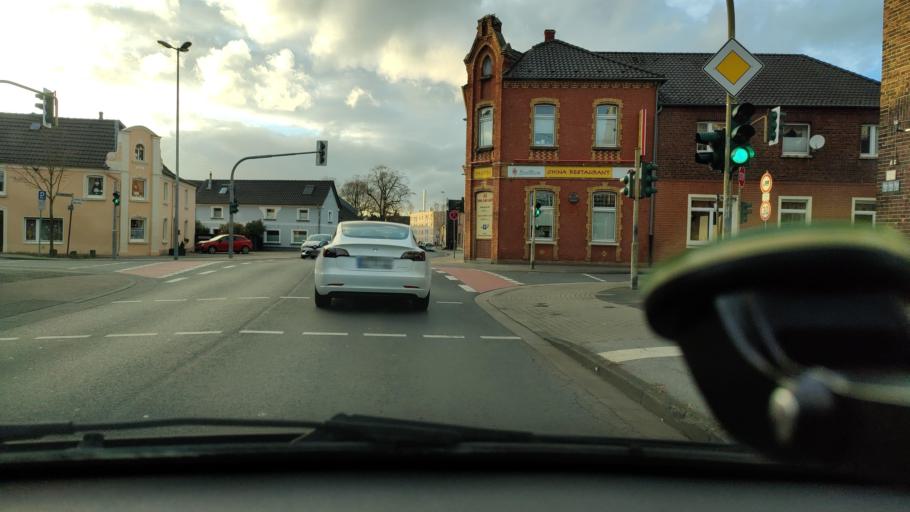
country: DE
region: North Rhine-Westphalia
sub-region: Regierungsbezirk Dusseldorf
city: Moers
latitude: 51.4895
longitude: 6.6091
